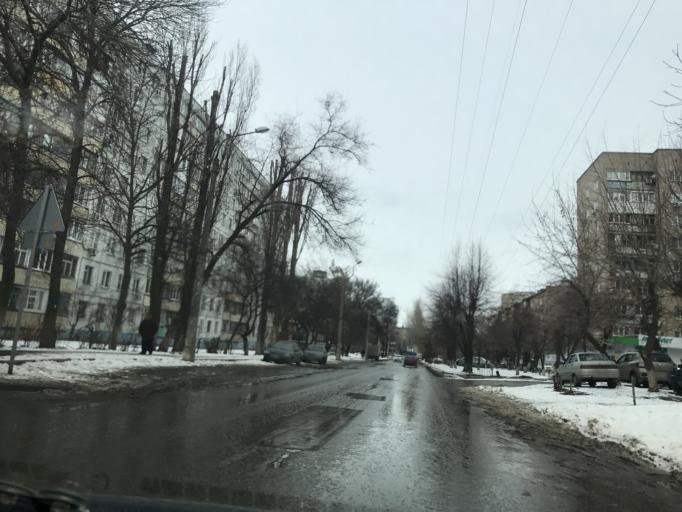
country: RU
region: Rostov
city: Rostov-na-Donu
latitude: 47.2298
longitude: 39.6334
